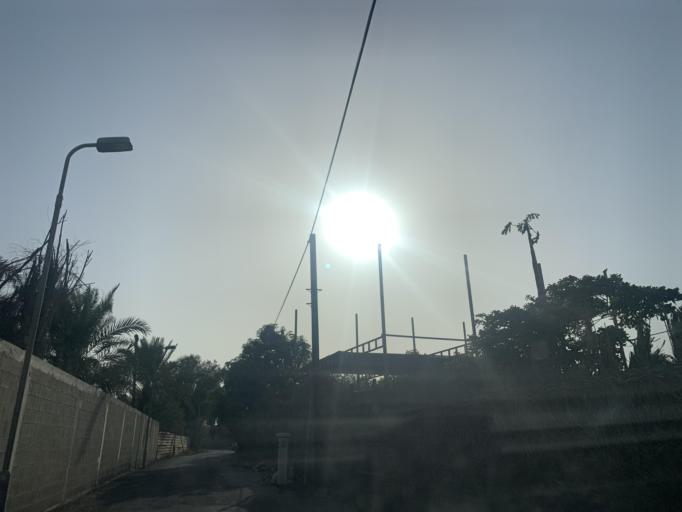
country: BH
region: Central Governorate
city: Madinat Hamad
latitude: 26.1880
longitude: 50.4617
